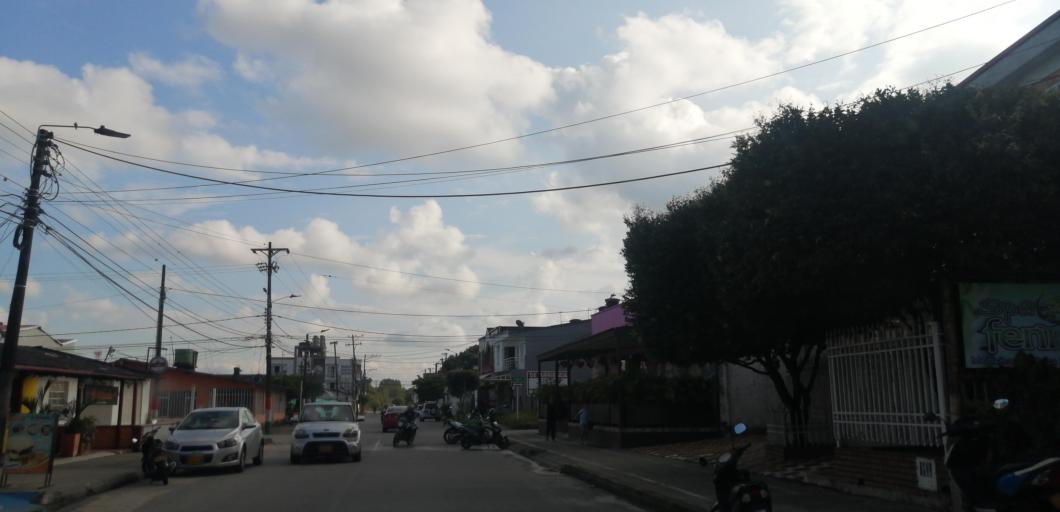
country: CO
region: Meta
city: Acacias
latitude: 3.9821
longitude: -73.7640
